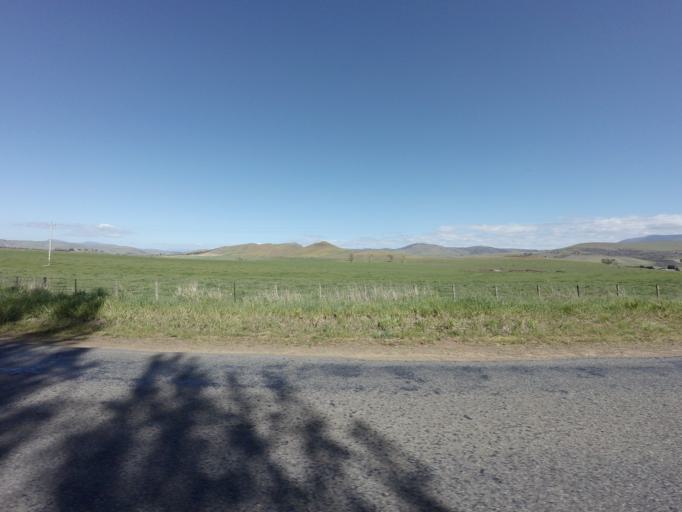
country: AU
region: Tasmania
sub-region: Derwent Valley
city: New Norfolk
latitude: -42.5385
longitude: 146.7583
